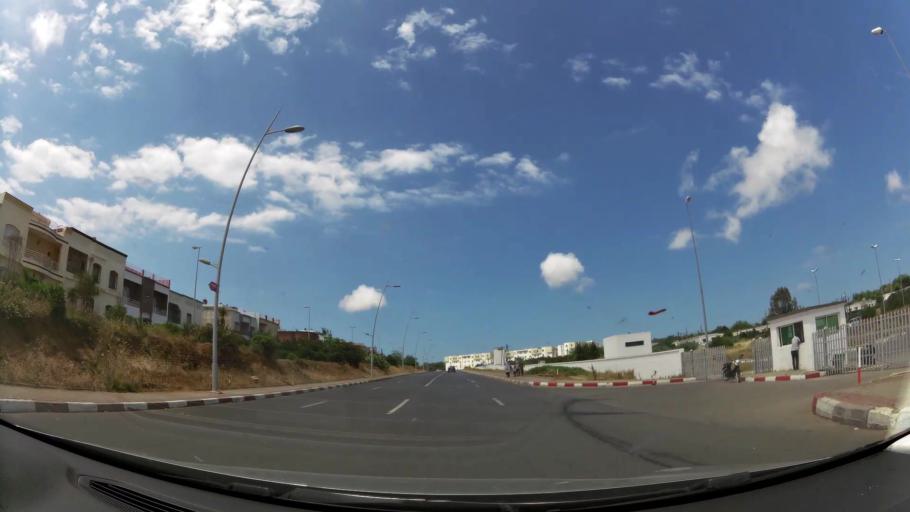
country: MA
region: Gharb-Chrarda-Beni Hssen
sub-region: Kenitra Province
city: Kenitra
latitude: 34.2774
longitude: -6.6071
